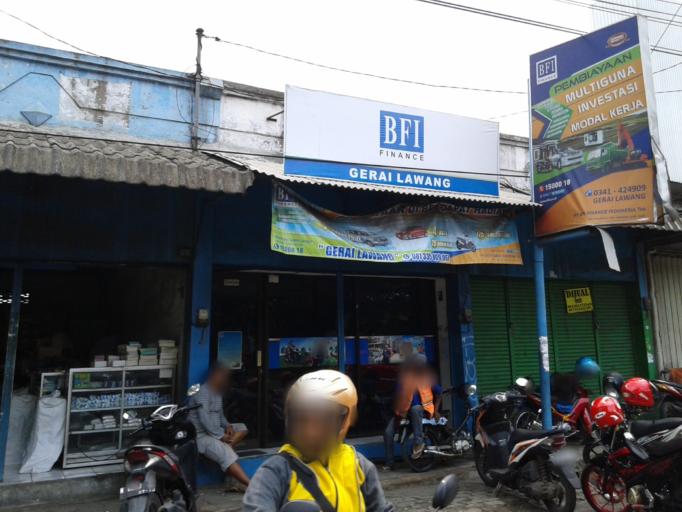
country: ID
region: East Java
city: Lawang
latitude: -7.8311
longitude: 112.6972
